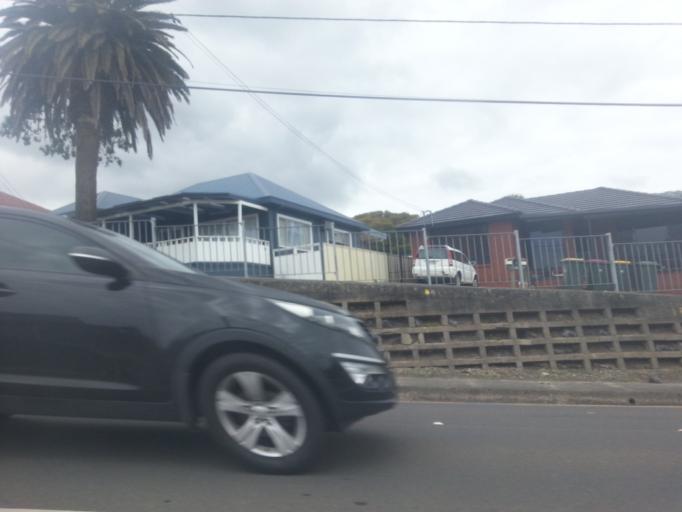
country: AU
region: New South Wales
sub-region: Wollongong
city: East Corrimal
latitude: -34.3574
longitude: 150.9005
